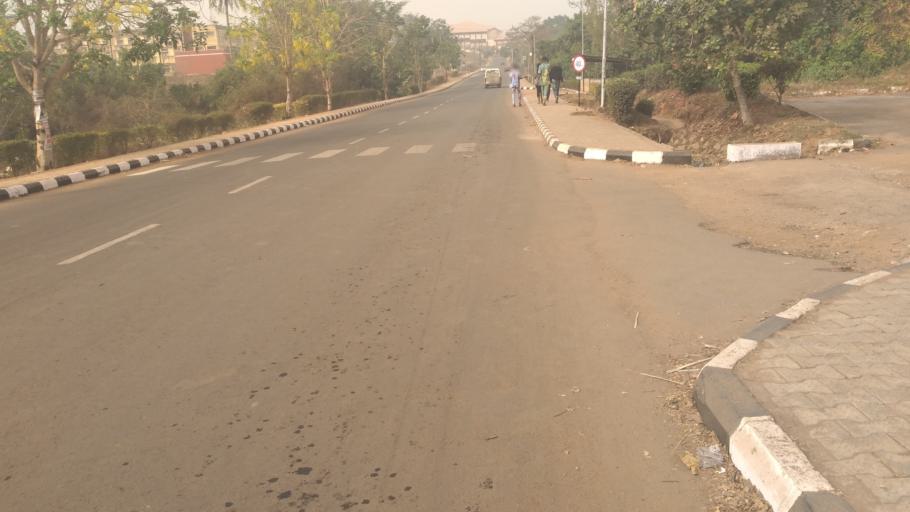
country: NG
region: Ondo
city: Ilare
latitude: 7.2994
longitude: 5.1356
